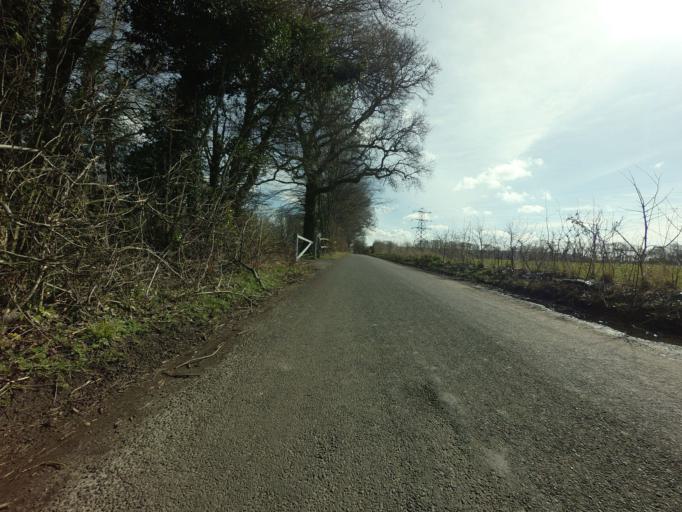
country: GB
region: England
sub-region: Kent
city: Shoreham
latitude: 51.3514
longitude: 0.1740
